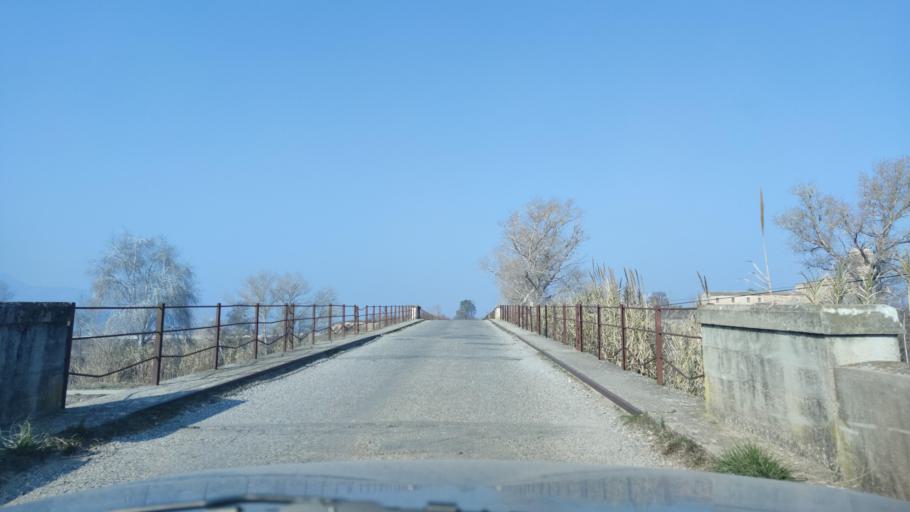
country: ES
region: Catalonia
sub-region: Provincia de Lleida
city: la Granja d'Escarp
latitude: 41.4291
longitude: 0.3549
